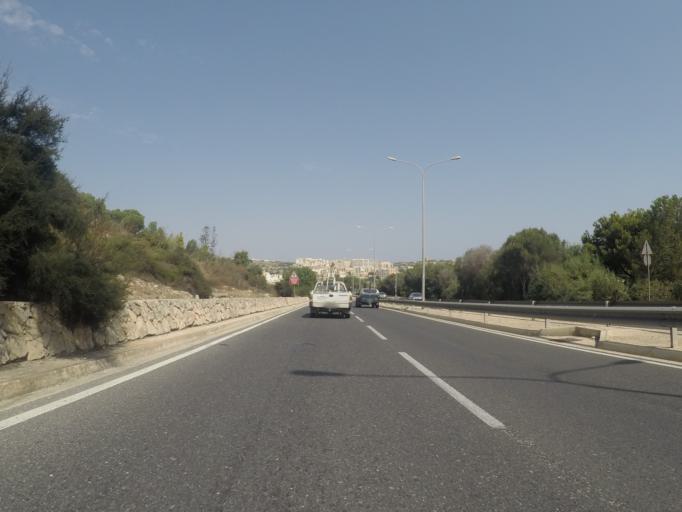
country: MT
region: Saint Paul's Bay
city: San Pawl il-Bahar
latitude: 35.9436
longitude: 14.3901
